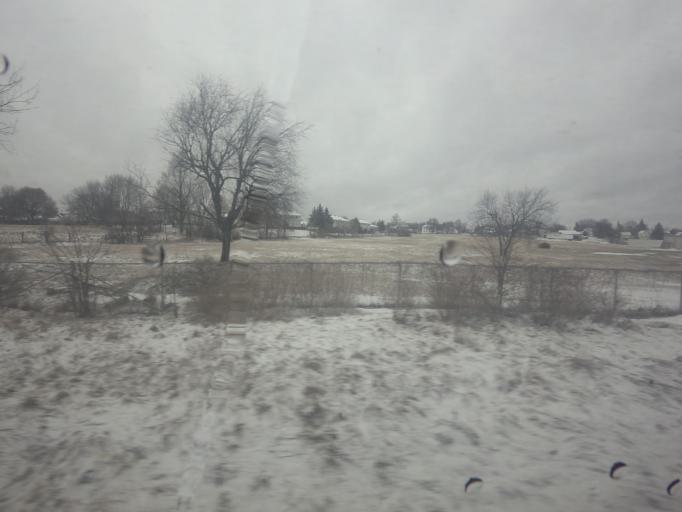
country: CA
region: Ontario
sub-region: Lanark County
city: Smiths Falls
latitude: 44.8997
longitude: -76.0080
